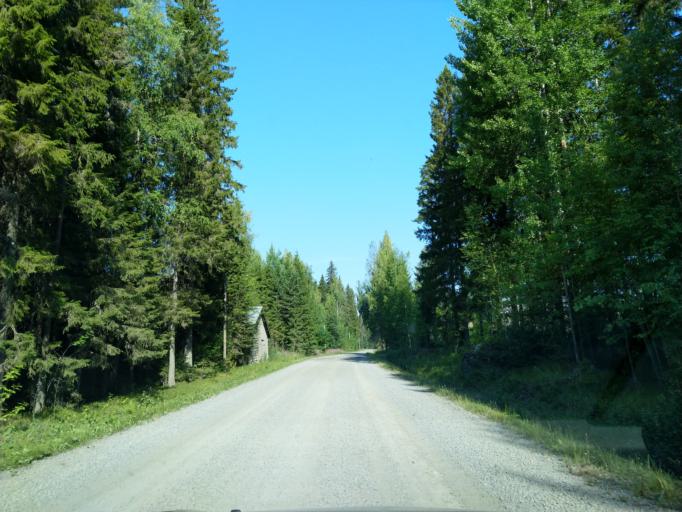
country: FI
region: Satakunta
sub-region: Pori
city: Laengelmaeki
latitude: 61.7325
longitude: 22.1738
